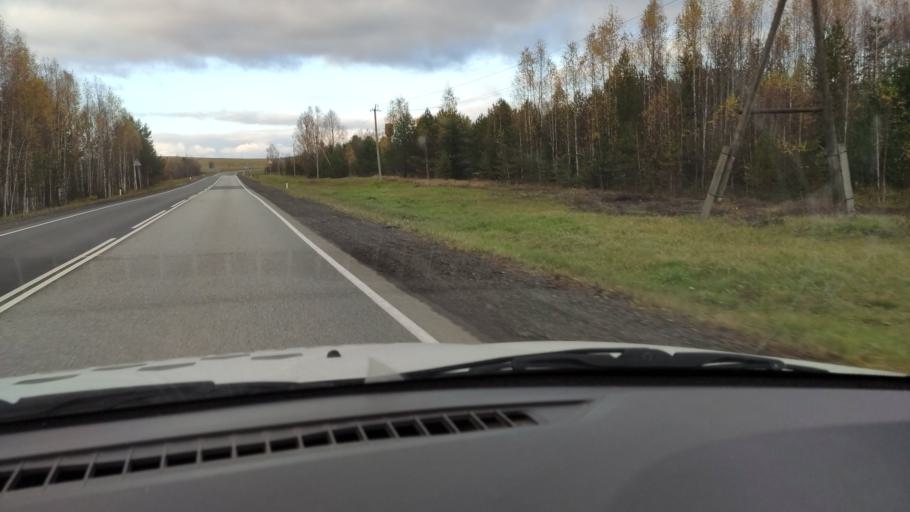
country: RU
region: Kirov
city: Belaya Kholunitsa
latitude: 58.8875
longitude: 50.8746
